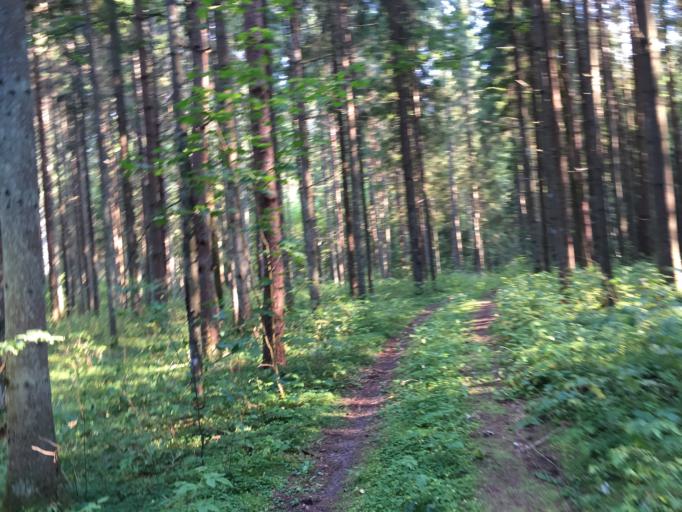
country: LV
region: Limbazu Rajons
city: Limbazi
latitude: 57.5656
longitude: 24.8002
